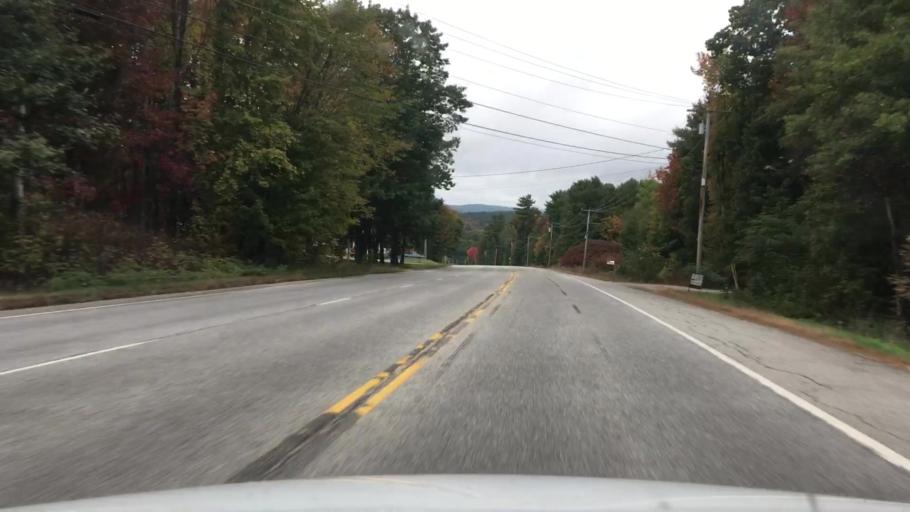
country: US
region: Maine
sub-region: Oxford County
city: Oxford
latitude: 44.1224
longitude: -70.4478
